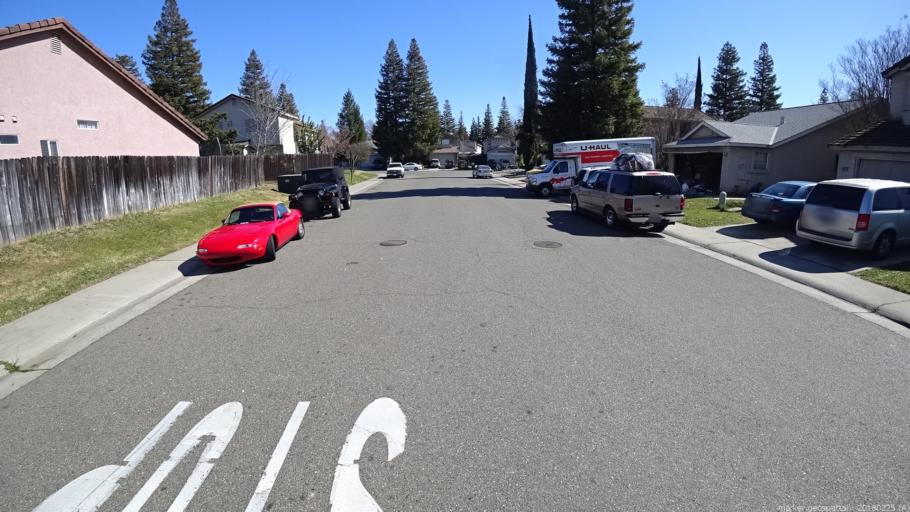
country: US
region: California
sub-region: Sacramento County
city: Antelope
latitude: 38.7209
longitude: -121.3580
